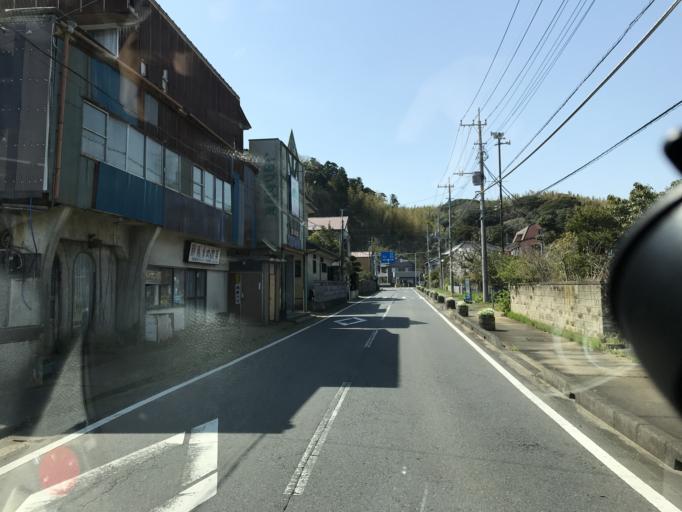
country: JP
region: Chiba
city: Asahi
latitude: 35.7825
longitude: 140.6523
